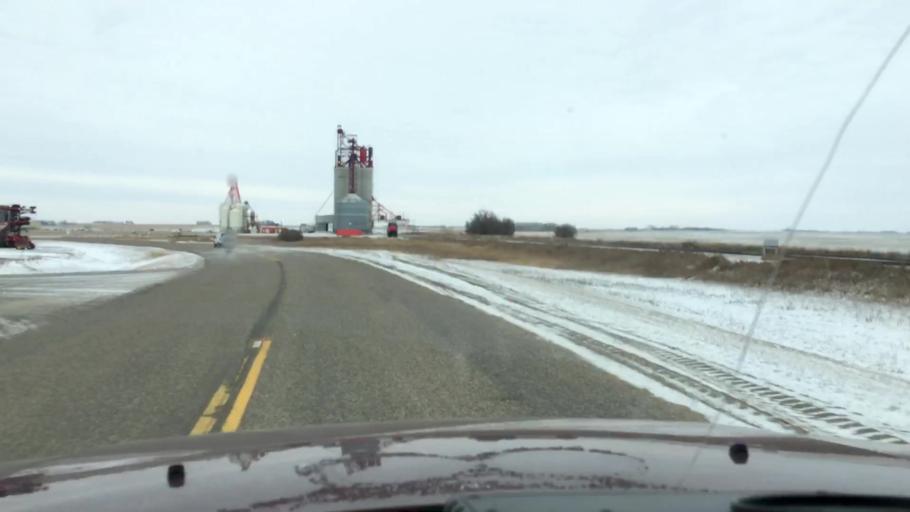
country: CA
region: Saskatchewan
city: Watrous
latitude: 51.2501
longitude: -105.9775
